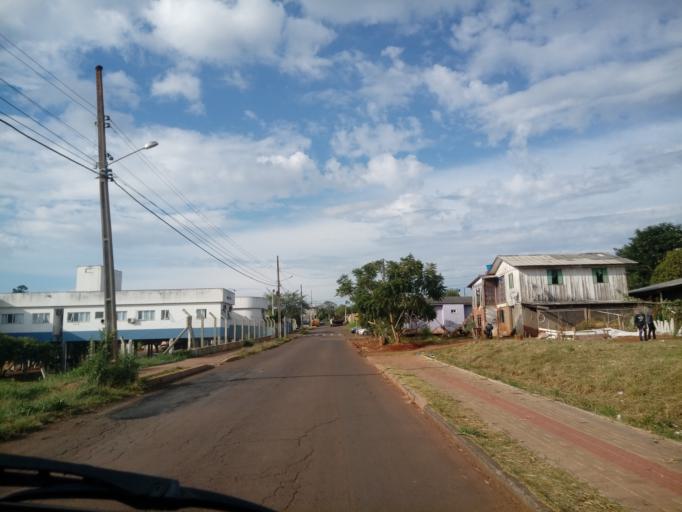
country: BR
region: Santa Catarina
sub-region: Chapeco
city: Chapeco
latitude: -27.1002
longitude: -52.5898
